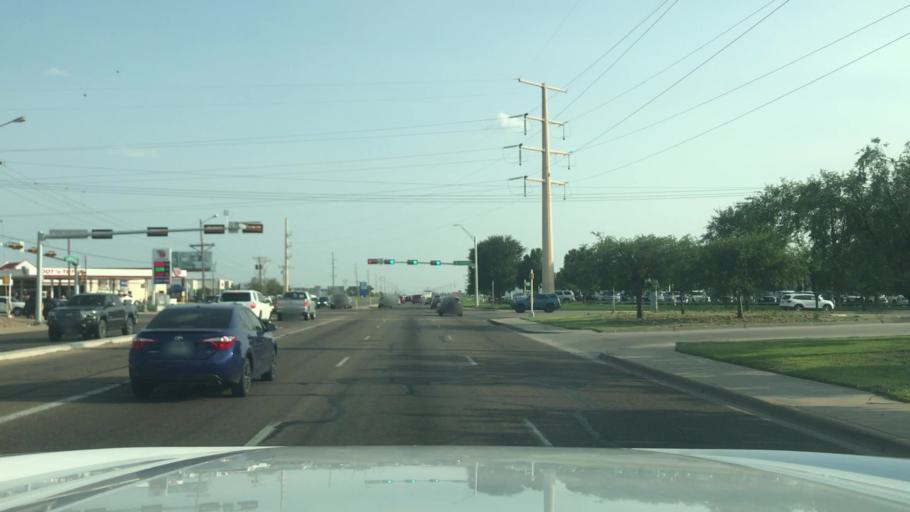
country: US
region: Texas
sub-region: Potter County
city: Amarillo
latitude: 35.1624
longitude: -101.9382
